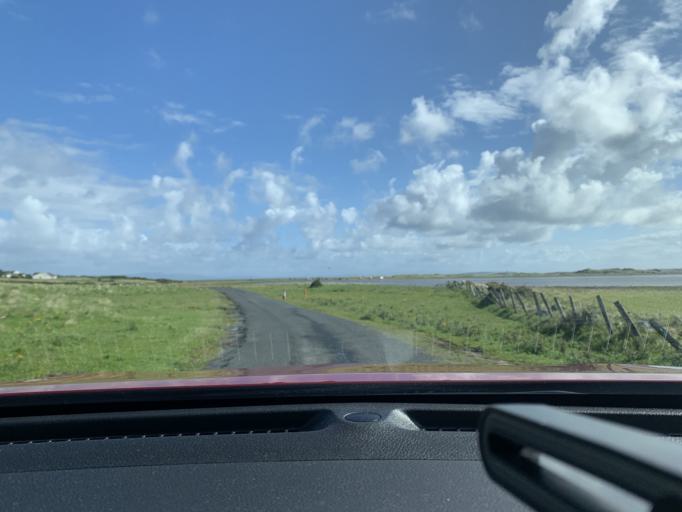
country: IE
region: Connaught
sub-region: Sligo
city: Strandhill
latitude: 54.3991
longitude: -8.5643
